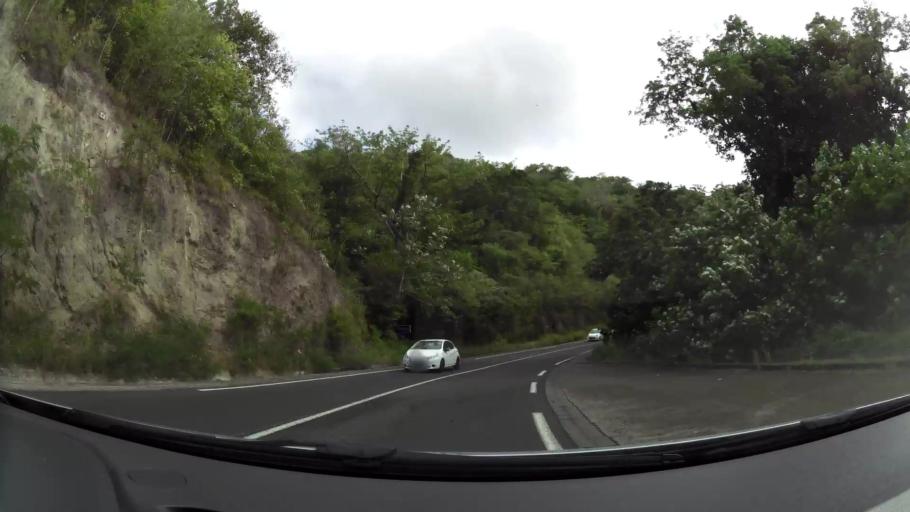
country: MQ
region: Martinique
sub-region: Martinique
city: Les Trois-Ilets
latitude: 14.4840
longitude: -61.0075
